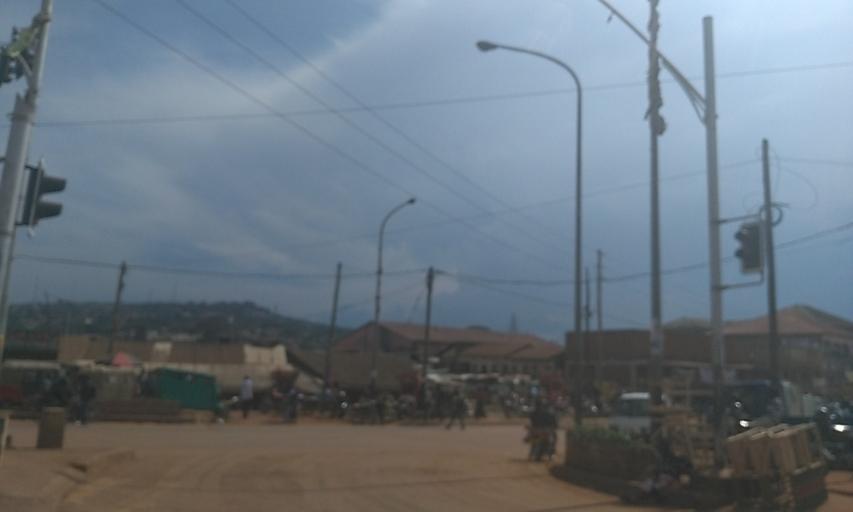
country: UG
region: Central Region
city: Kampala Central Division
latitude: 0.2996
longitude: 32.5326
